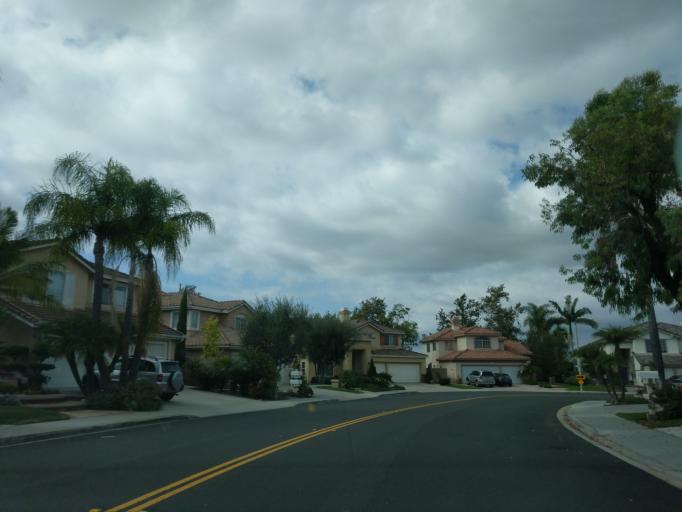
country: US
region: California
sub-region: Orange County
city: Laguna Woods
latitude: 33.5987
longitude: -117.7365
